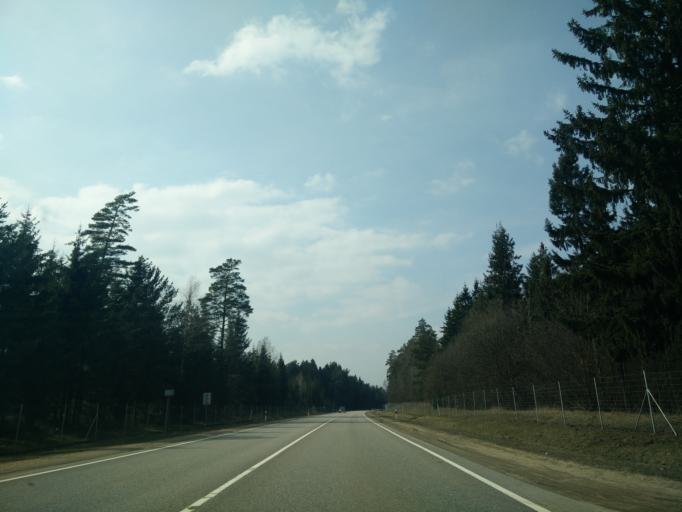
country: LT
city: Lentvaris
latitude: 54.6196
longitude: 25.0882
